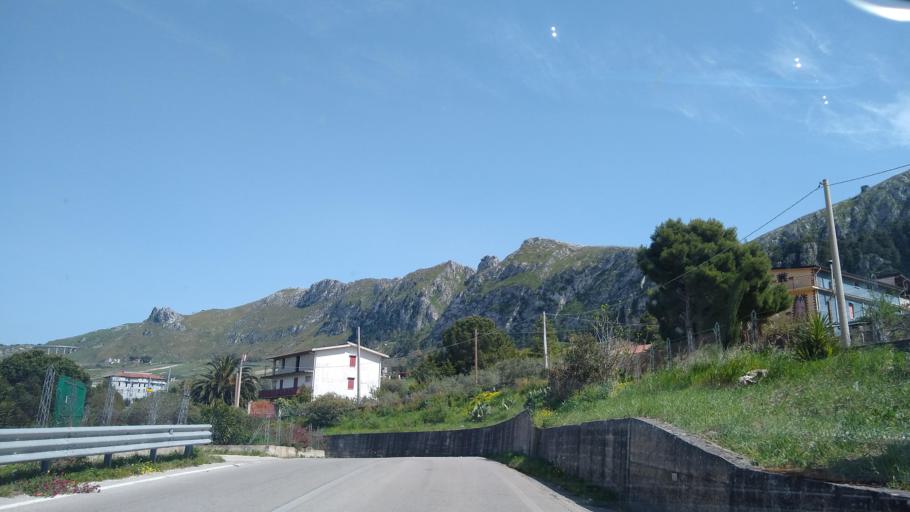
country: IT
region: Sicily
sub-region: Palermo
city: San Giuseppe Jato
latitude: 37.9753
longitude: 13.2021
